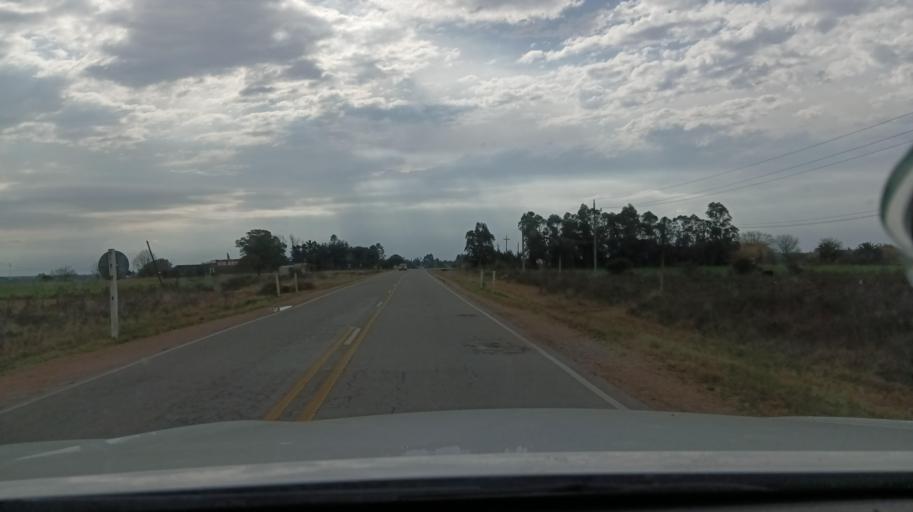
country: UY
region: Canelones
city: Toledo
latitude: -34.6970
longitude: -56.1066
